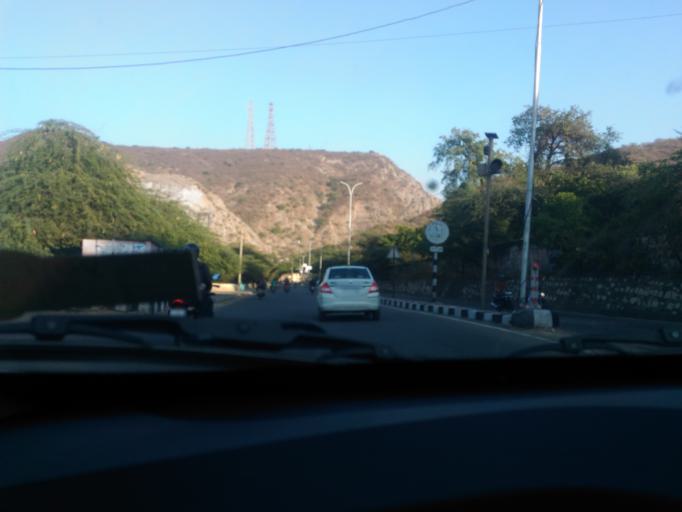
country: IN
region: Rajasthan
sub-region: Jaipur
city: Jaipur
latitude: 26.9016
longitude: 75.8483
